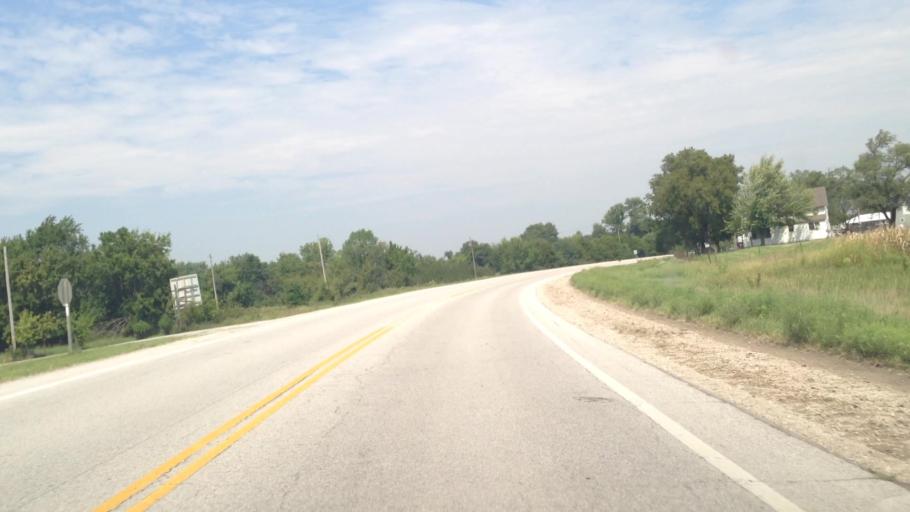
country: US
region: Kansas
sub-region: Labette County
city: Parsons
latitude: 37.3906
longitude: -95.2696
